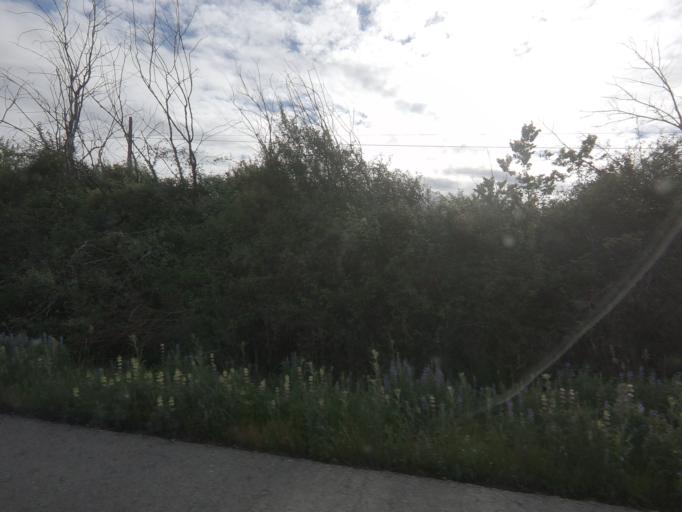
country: ES
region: Extremadura
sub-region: Provincia de Caceres
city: Moraleja
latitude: 40.0924
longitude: -6.6741
